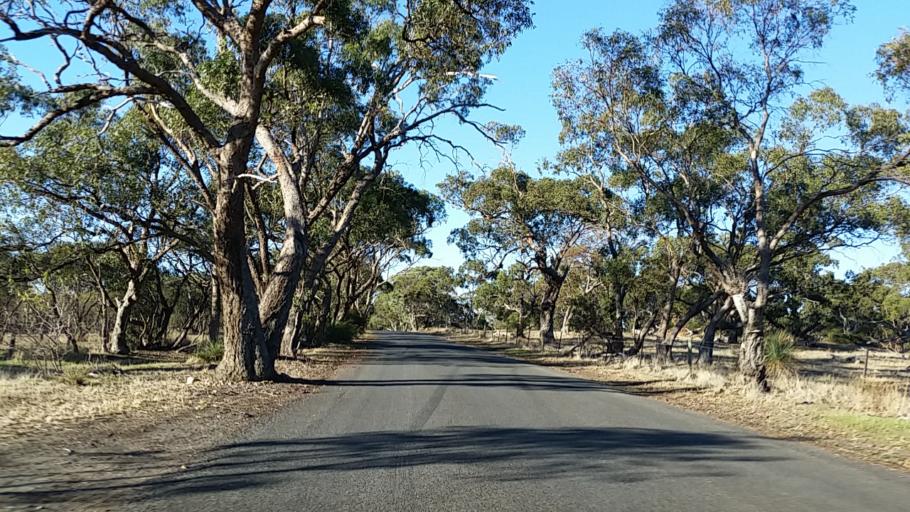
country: AU
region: South Australia
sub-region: Onkaparinga
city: Hackham
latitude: -35.1562
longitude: 138.5458
